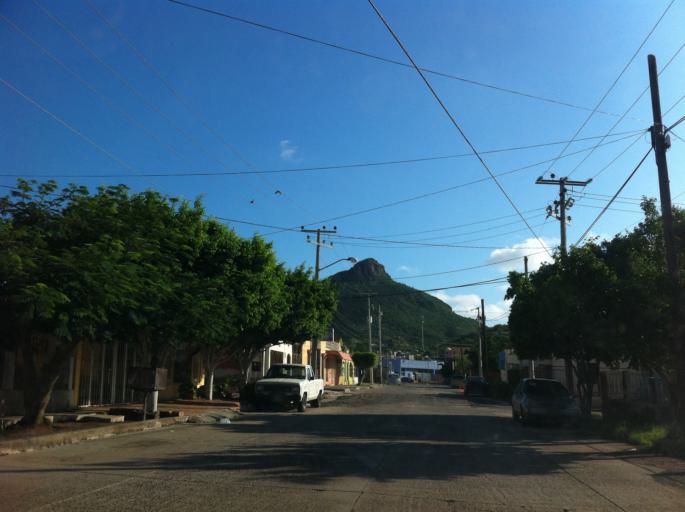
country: MX
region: Sonora
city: Heroica Guaymas
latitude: 27.9227
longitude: -110.9165
